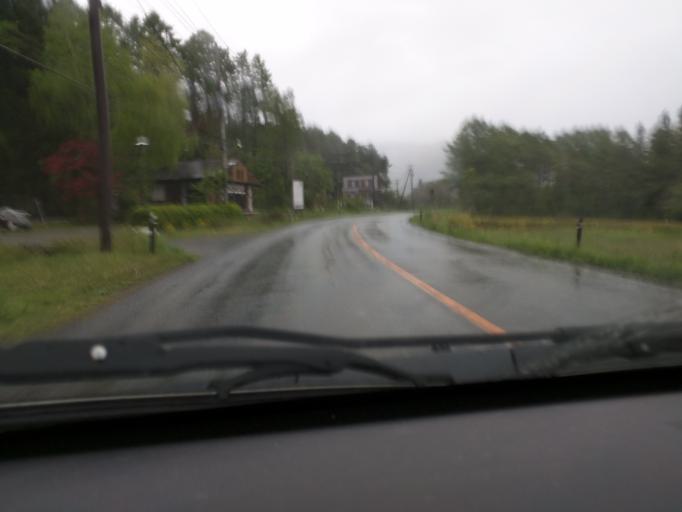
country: JP
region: Fukushima
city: Inawashiro
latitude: 37.5912
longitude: 140.1249
